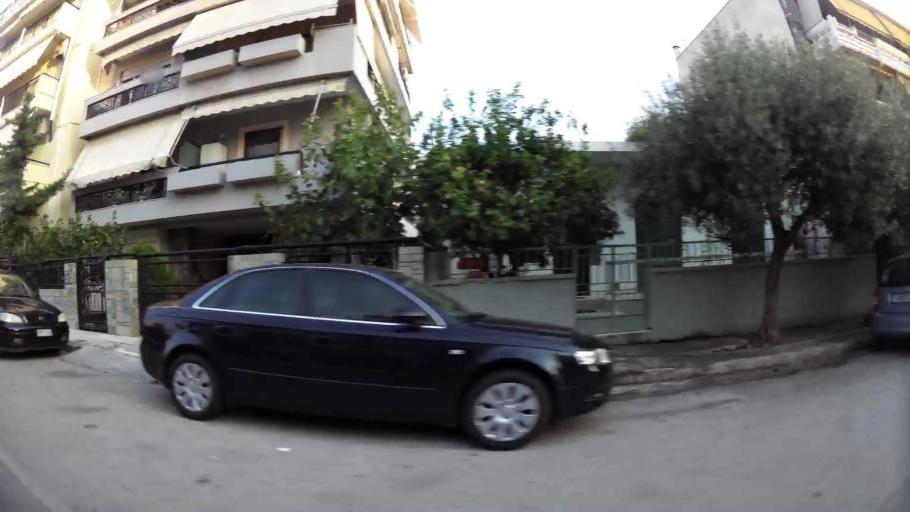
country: GR
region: Attica
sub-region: Nomarchia Athinas
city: Petroupolis
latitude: 38.0429
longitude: 23.6906
